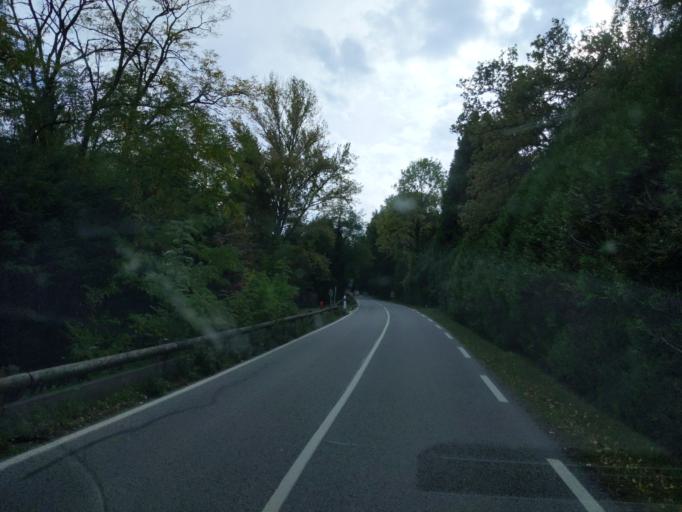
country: FR
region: Ile-de-France
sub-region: Departement des Yvelines
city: Chevreuse
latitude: 48.6887
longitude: 2.0141
